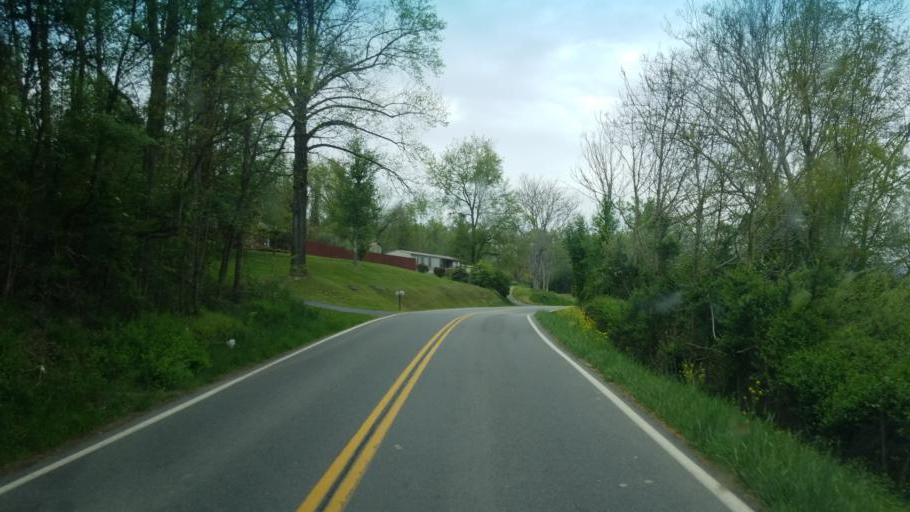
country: US
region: Virginia
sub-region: Smyth County
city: Adwolf
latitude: 36.8048
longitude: -81.5777
